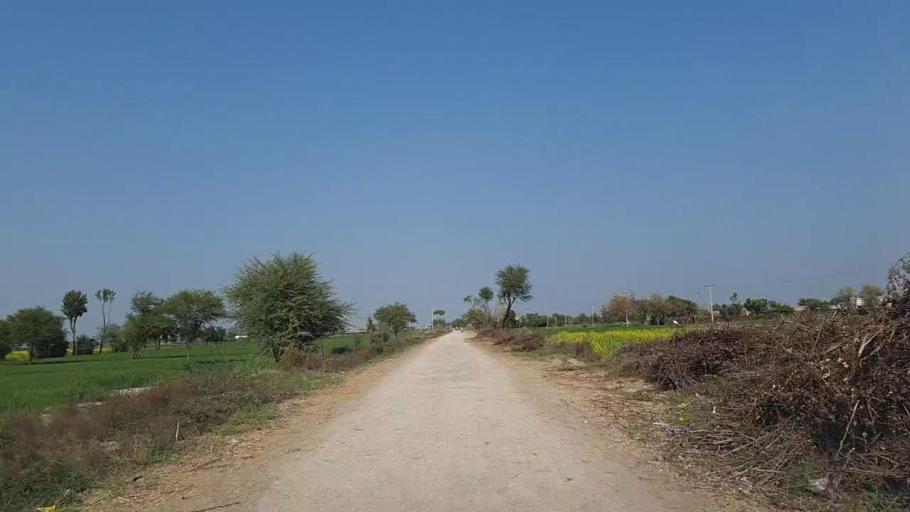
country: PK
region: Sindh
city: Nawabshah
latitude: 26.2830
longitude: 68.5136
